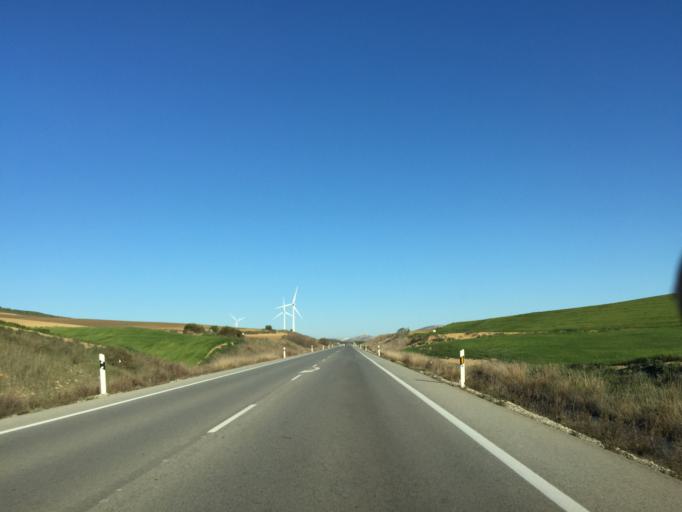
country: ES
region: Andalusia
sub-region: Provincia de Malaga
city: Ardales
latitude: 36.9253
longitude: -4.8490
